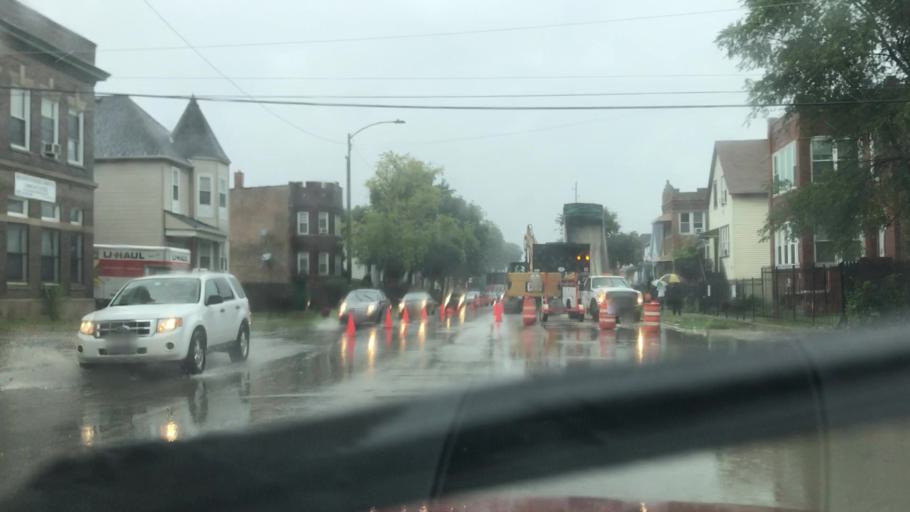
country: US
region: Illinois
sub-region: Cook County
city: Oak Park
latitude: 41.8952
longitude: -87.7556
